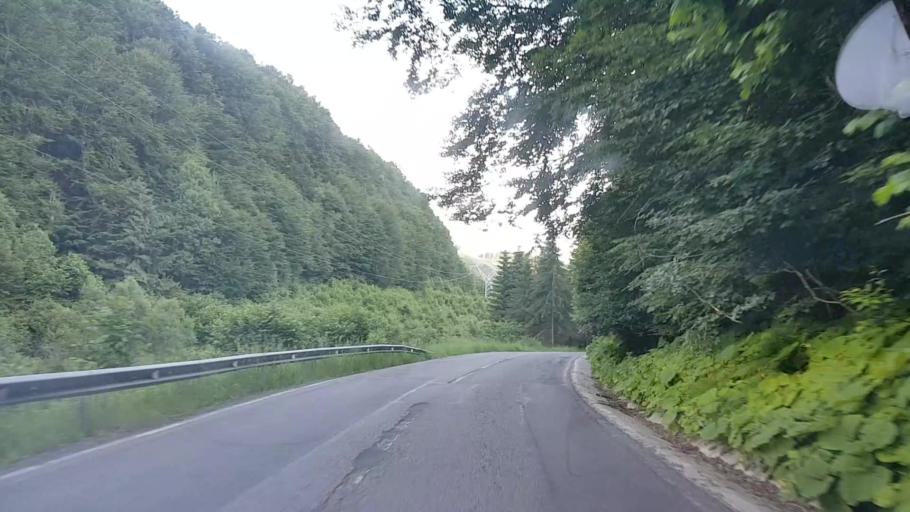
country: RO
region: Harghita
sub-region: Comuna Praid
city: Ocna de Sus
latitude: 46.5993
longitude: 25.2392
